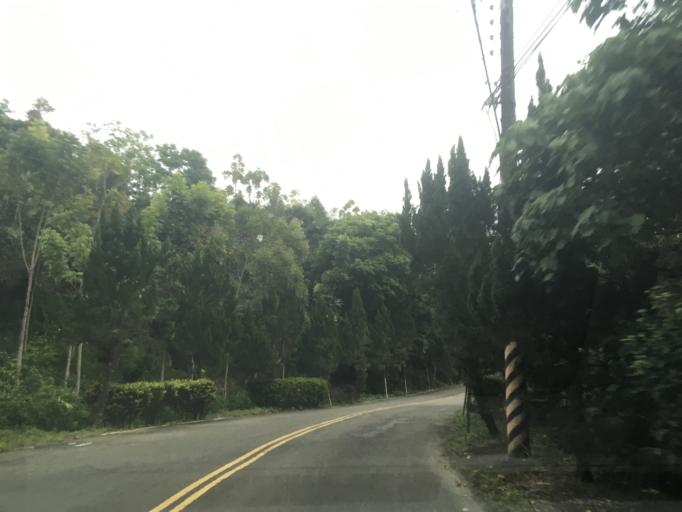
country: TW
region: Taiwan
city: Zhongxing New Village
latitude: 24.0344
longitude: 120.7430
